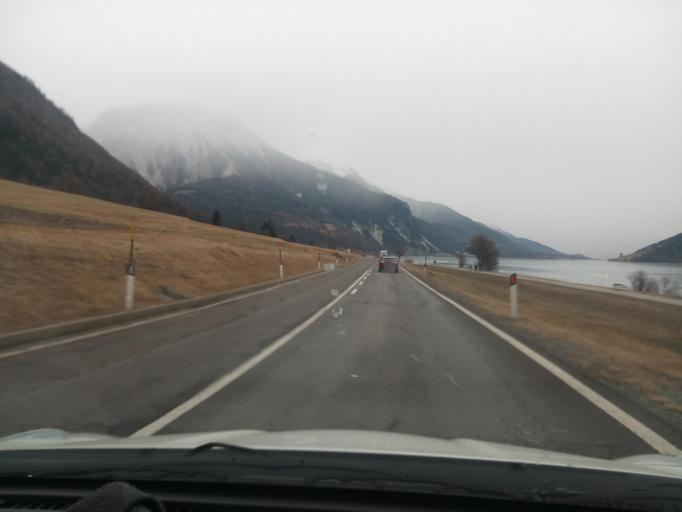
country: IT
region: Trentino-Alto Adige
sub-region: Bolzano
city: Curon Venosta
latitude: 46.8224
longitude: 10.5220
